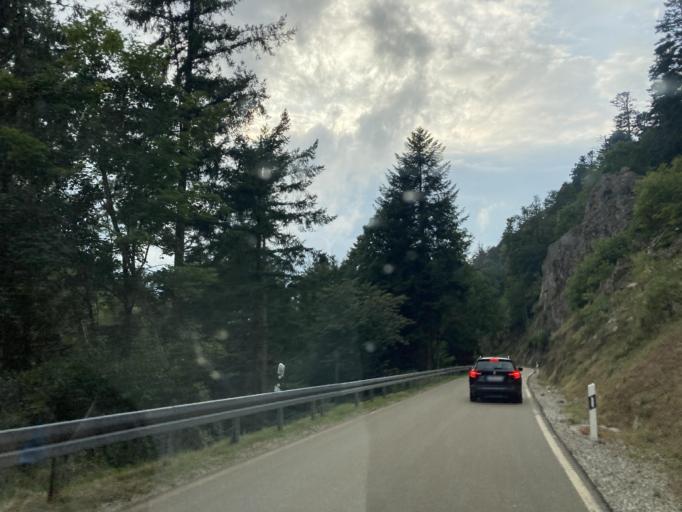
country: DE
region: Baden-Wuerttemberg
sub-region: Freiburg Region
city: Sulzburg
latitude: 47.8008
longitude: 7.7464
